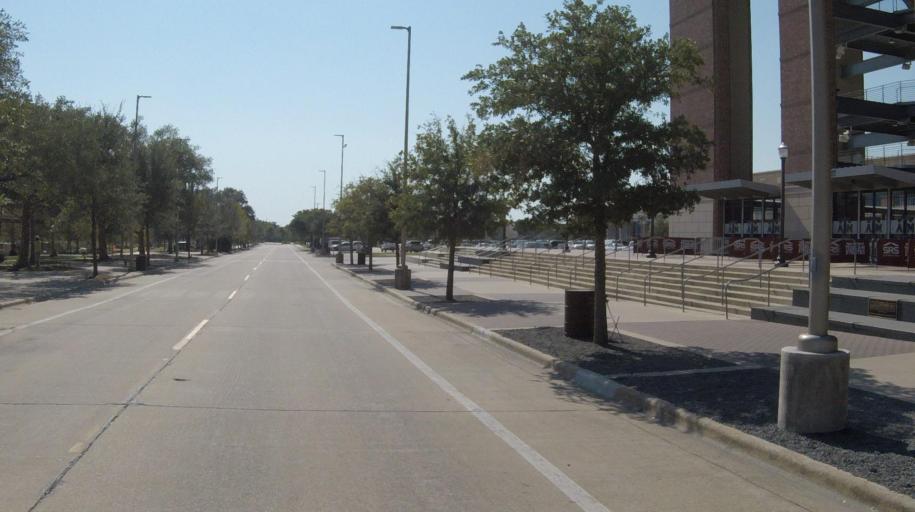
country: US
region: Texas
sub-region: Brazos County
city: College Station
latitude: 30.6103
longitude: -96.3389
